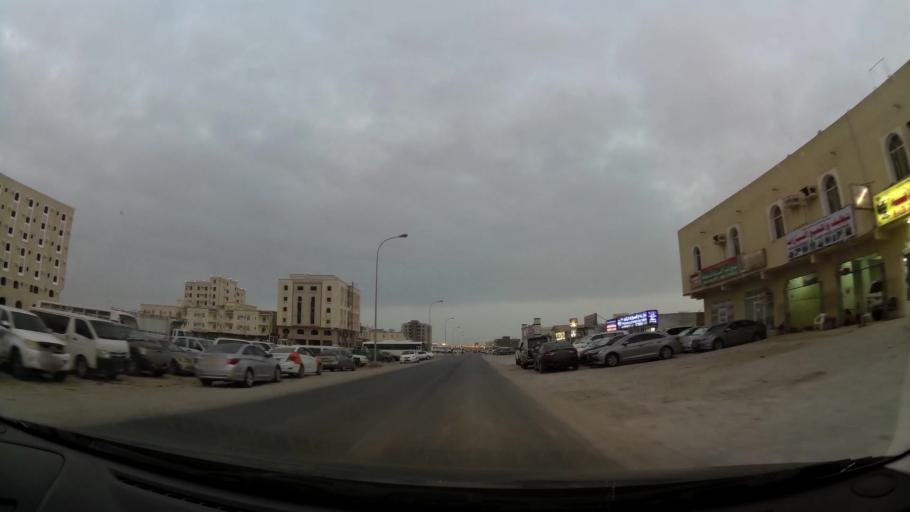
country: OM
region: Zufar
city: Salalah
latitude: 17.0271
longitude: 54.0533
